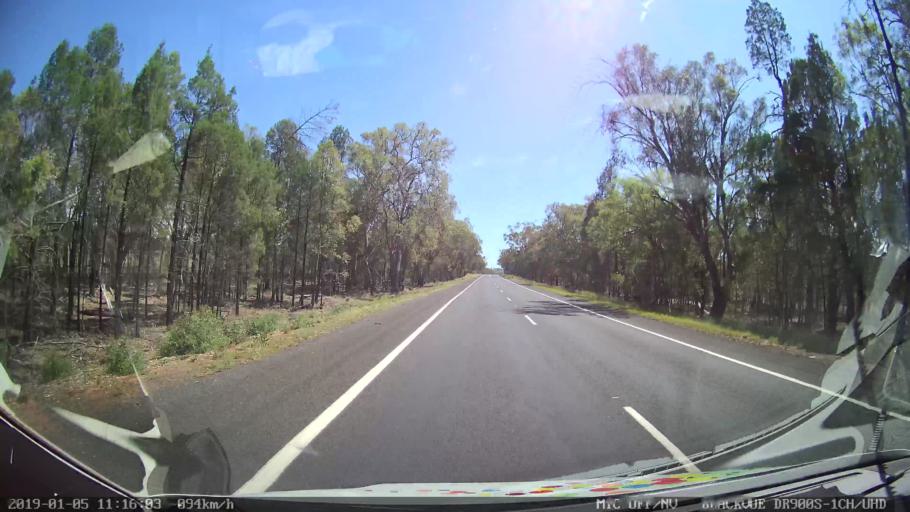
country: AU
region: New South Wales
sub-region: Warrumbungle Shire
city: Coonabarabran
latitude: -31.3443
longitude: 149.2964
